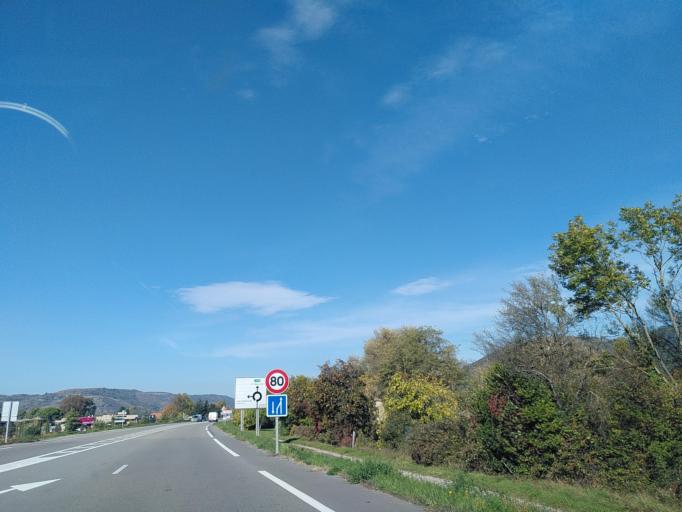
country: FR
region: Rhone-Alpes
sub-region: Departement de la Drome
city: Saint-Vallier
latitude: 45.1705
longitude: 4.8150
